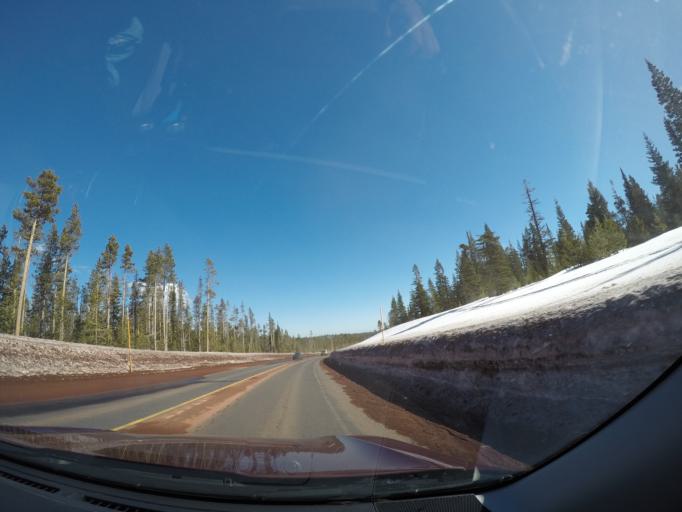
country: US
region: Oregon
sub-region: Deschutes County
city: Sunriver
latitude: 43.9850
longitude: -121.5782
